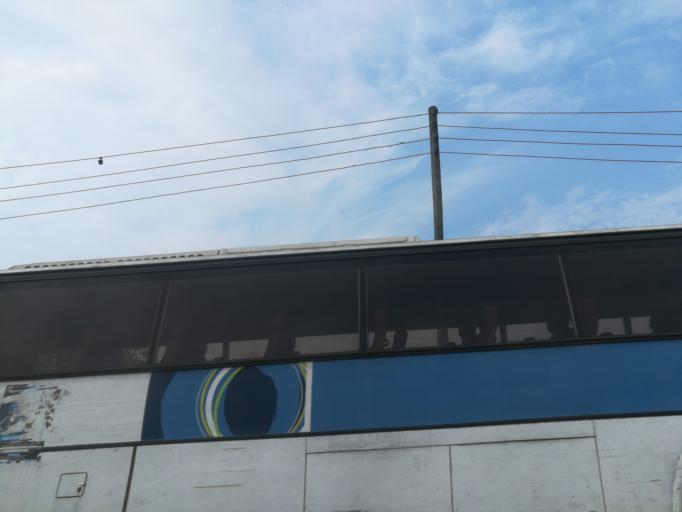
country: NG
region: Rivers
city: Okrika
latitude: 4.7625
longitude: 7.0879
